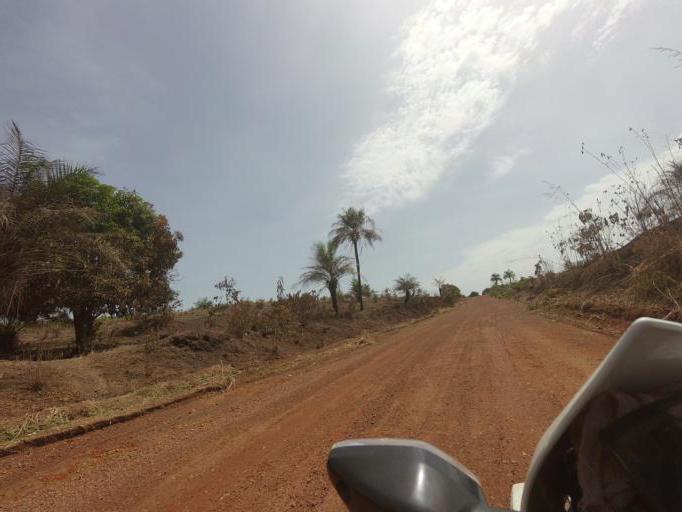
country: SL
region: Northern Province
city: Kamakwie
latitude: 9.4375
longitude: -12.2516
